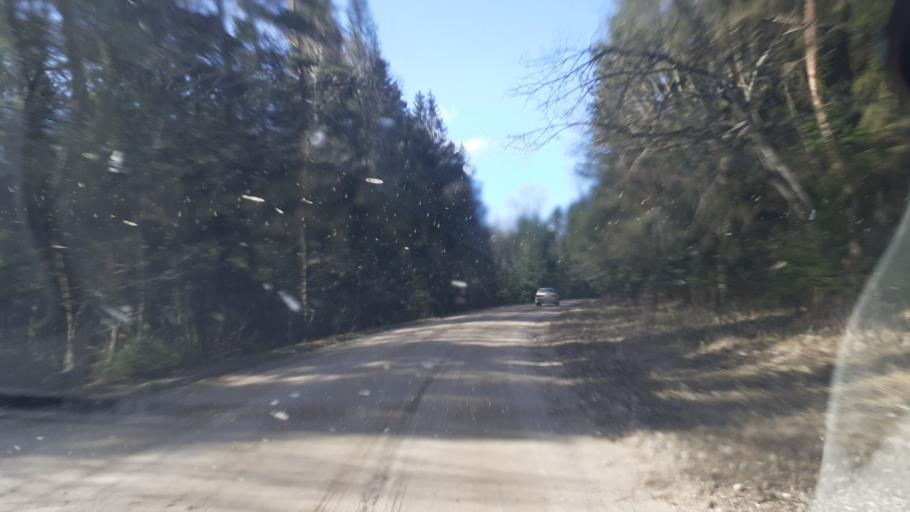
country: LV
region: Kuldigas Rajons
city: Kuldiga
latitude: 56.9104
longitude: 22.0806
